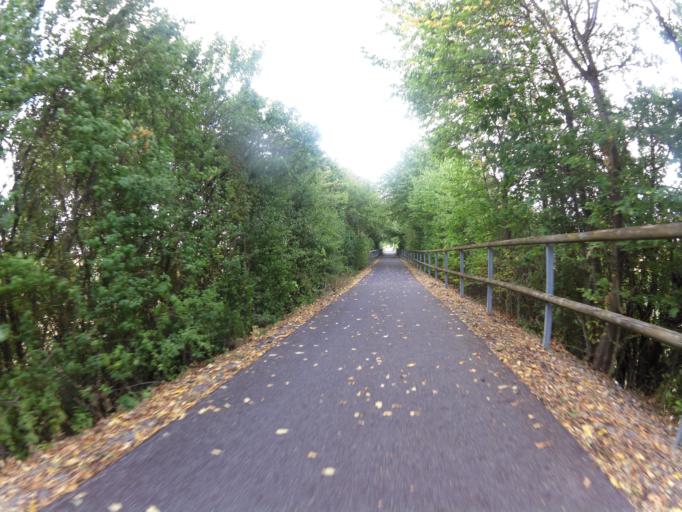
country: DE
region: Bavaria
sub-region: Regierungsbezirk Unterfranken
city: Sonderhofen
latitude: 49.5885
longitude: 10.0077
